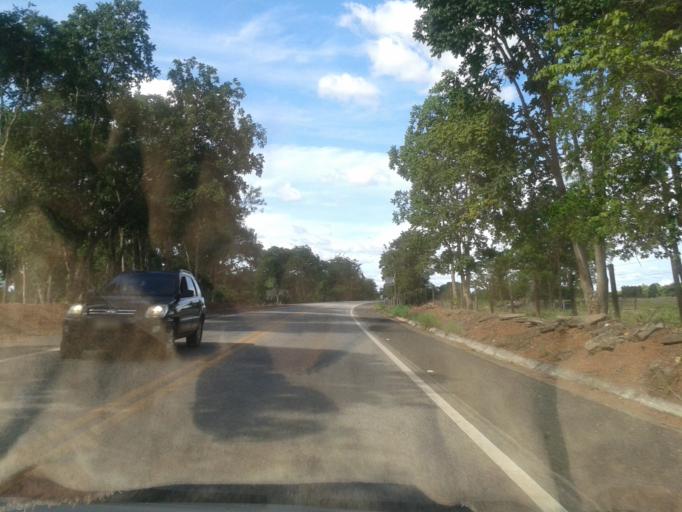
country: BR
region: Goias
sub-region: Mozarlandia
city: Mozarlandia
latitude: -14.9929
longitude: -50.5860
